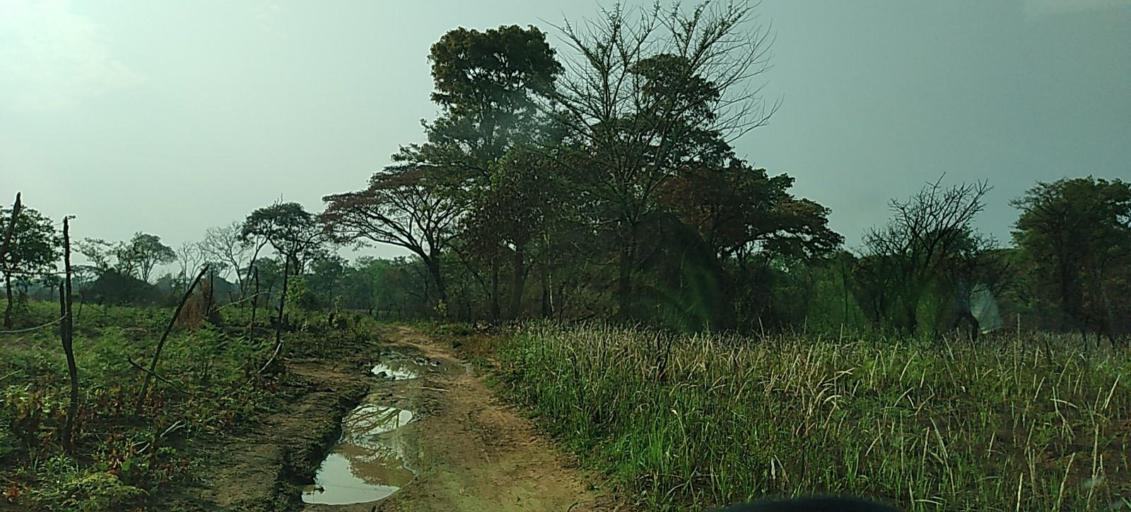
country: ZM
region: North-Western
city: Solwezi
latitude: -12.3872
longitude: 26.5696
